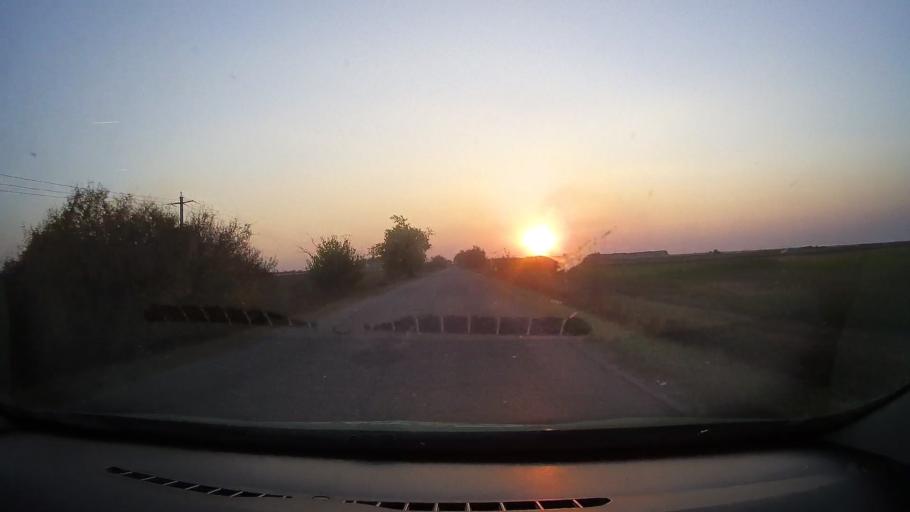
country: RO
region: Arad
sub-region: Comuna Olari
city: Olari
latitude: 46.4050
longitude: 21.5814
